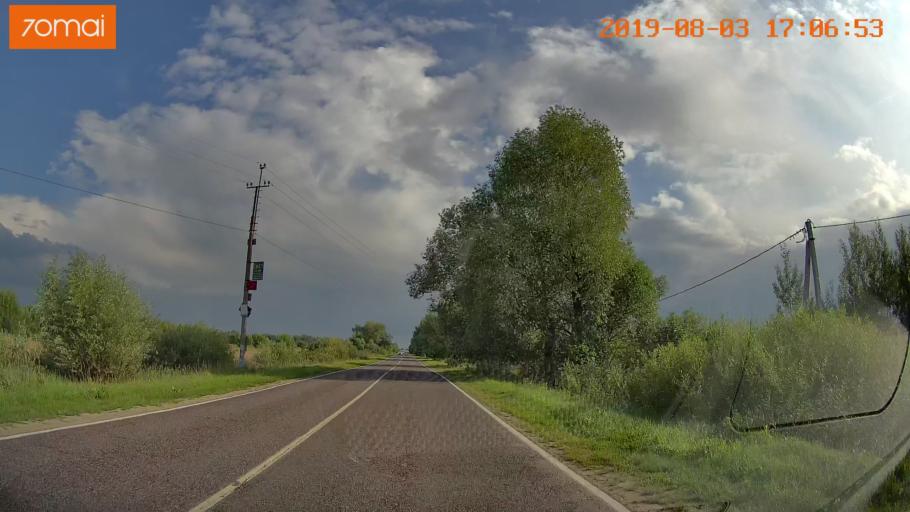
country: RU
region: Moskovskaya
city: Troitskoye
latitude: 55.3032
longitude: 38.5485
